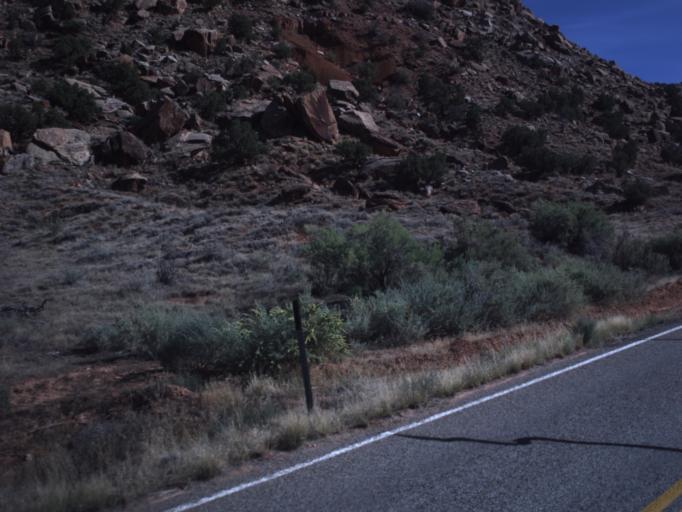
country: US
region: Utah
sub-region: San Juan County
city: Monticello
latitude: 38.0500
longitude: -109.5529
